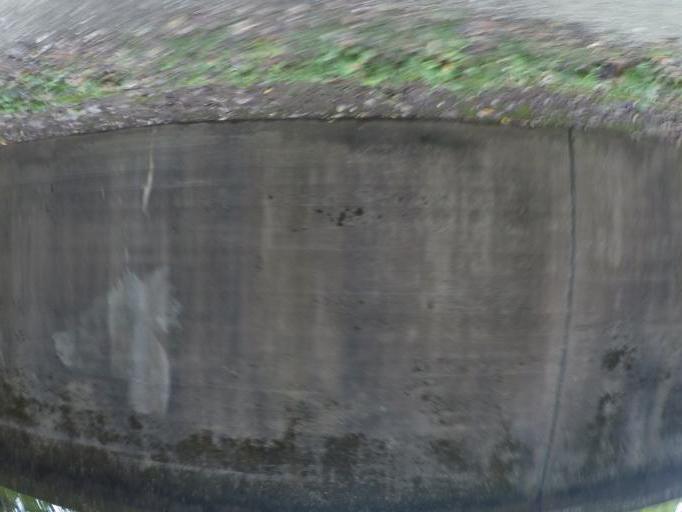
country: US
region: West Virginia
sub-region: Cabell County
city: Huntington
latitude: 38.4262
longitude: -82.3903
